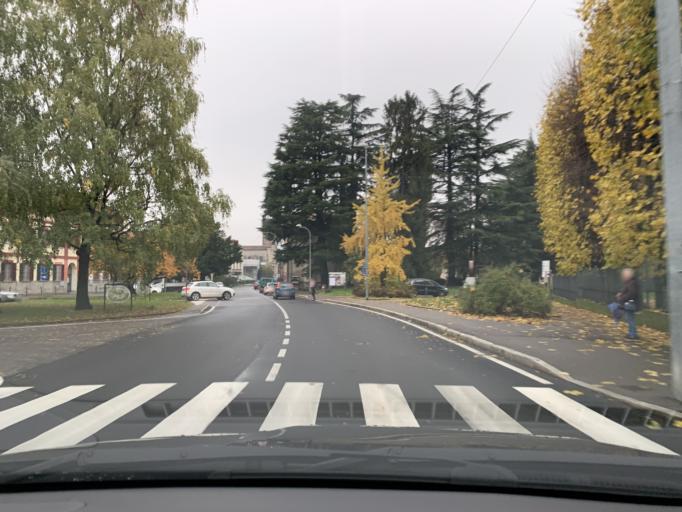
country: IT
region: Lombardy
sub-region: Provincia di Como
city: Rovellasca
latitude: 45.6695
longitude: 9.0536
